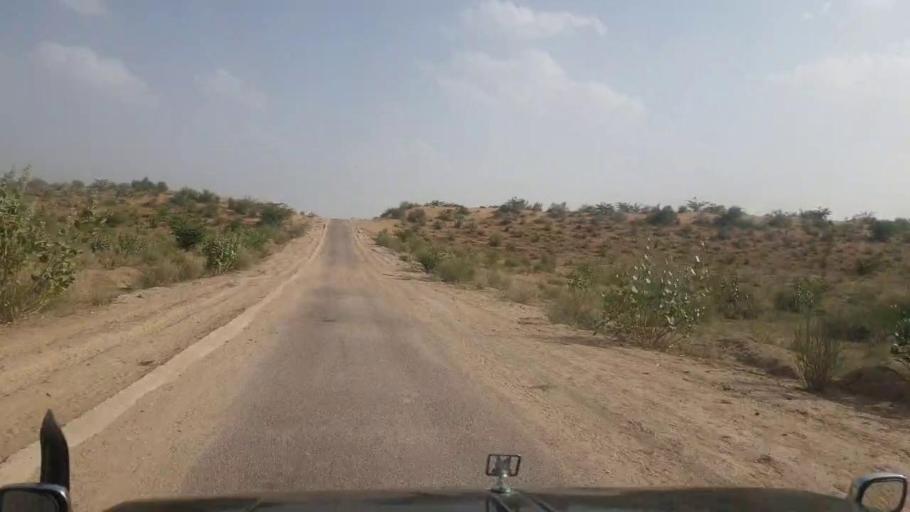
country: PK
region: Sindh
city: Islamkot
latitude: 25.1414
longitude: 70.3163
